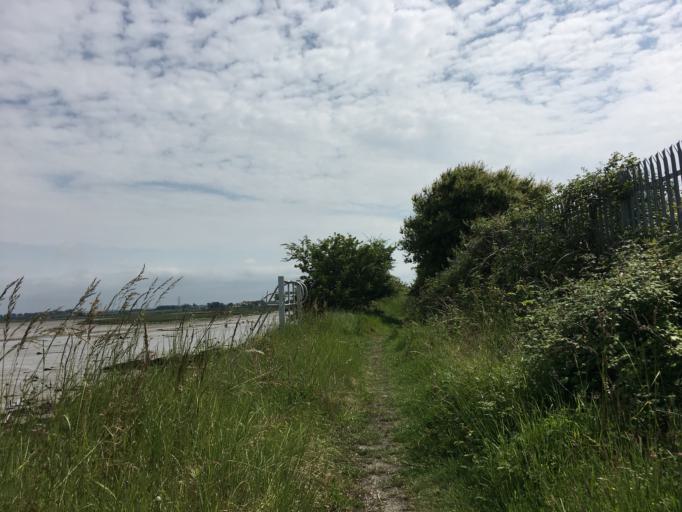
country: GB
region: England
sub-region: Kent
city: Sittingbourne
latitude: 51.3675
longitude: 0.7630
